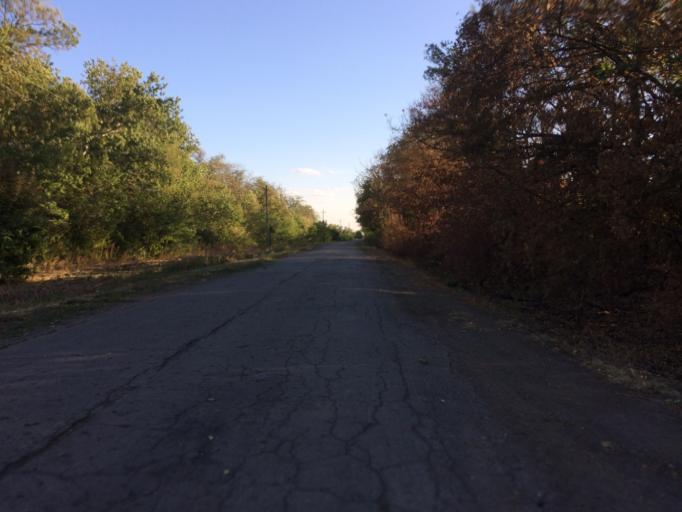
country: RU
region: Rostov
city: Gigant
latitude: 46.5125
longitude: 41.1921
